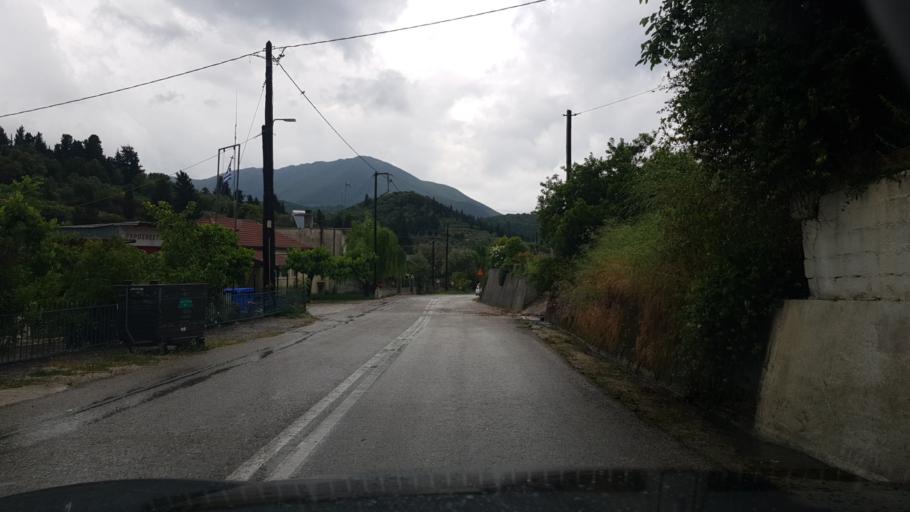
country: GR
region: Ionian Islands
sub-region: Lefkada
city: Nidri
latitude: 38.6284
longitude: 20.6297
